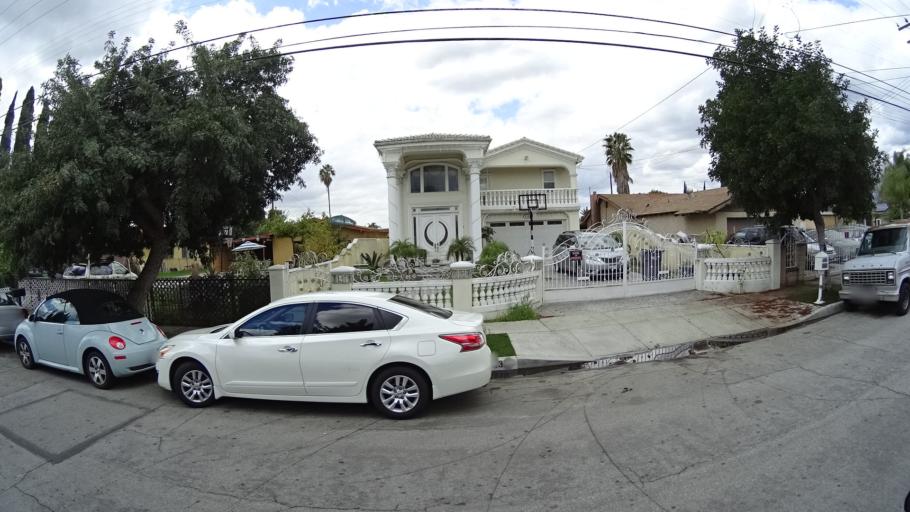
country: US
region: California
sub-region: Los Angeles County
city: Baldwin Park
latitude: 34.0870
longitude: -117.9780
